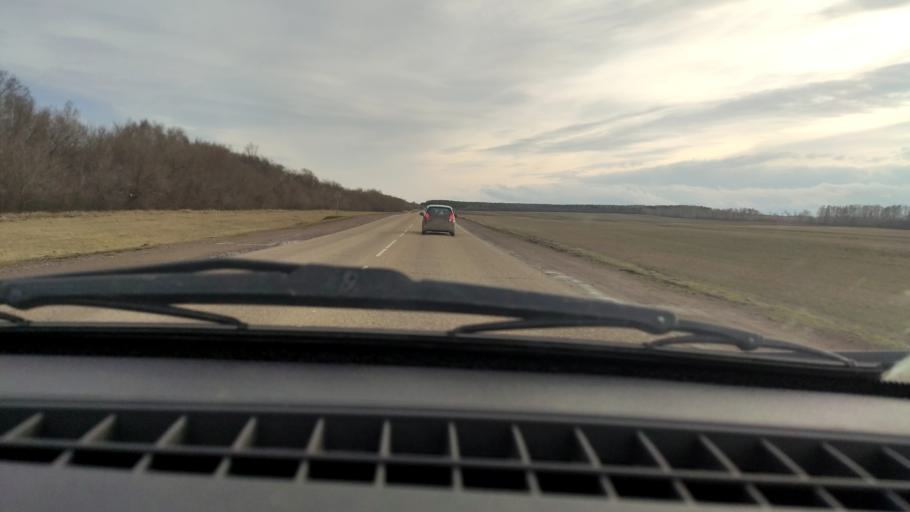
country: RU
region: Bashkortostan
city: Davlekanovo
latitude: 54.2573
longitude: 55.0868
